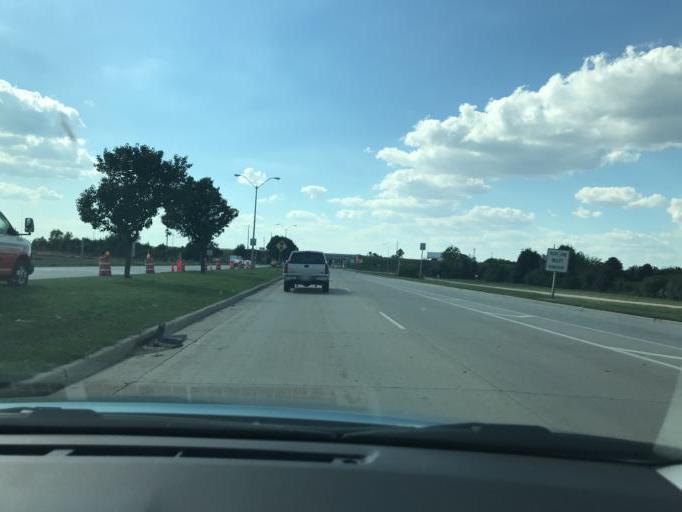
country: US
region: Wisconsin
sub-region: Walworth County
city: Delavan
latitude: 42.6277
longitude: -88.6143
